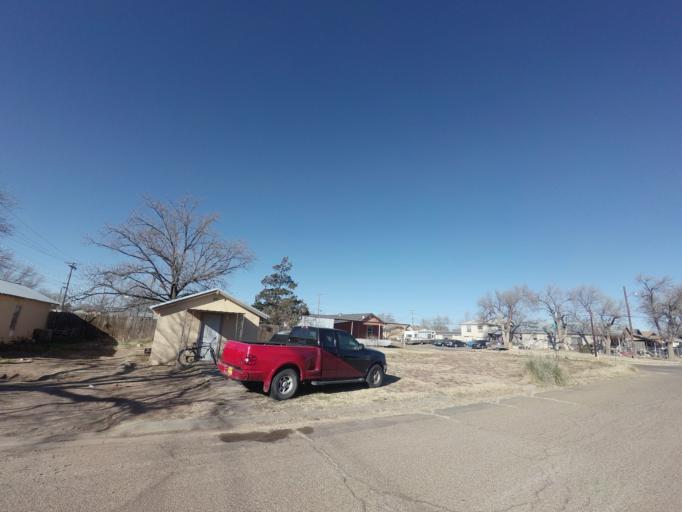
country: US
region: New Mexico
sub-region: Curry County
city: Clovis
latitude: 34.4015
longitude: -103.1915
